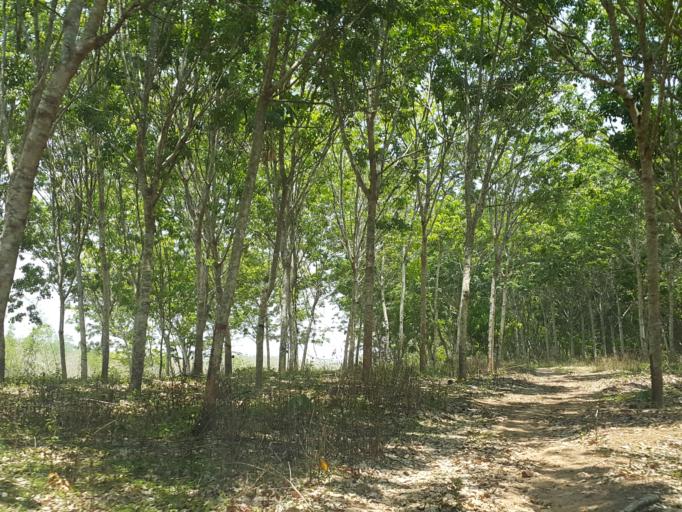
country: TH
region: Kanchanaburi
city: Sai Yok
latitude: 14.2357
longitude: 98.8662
